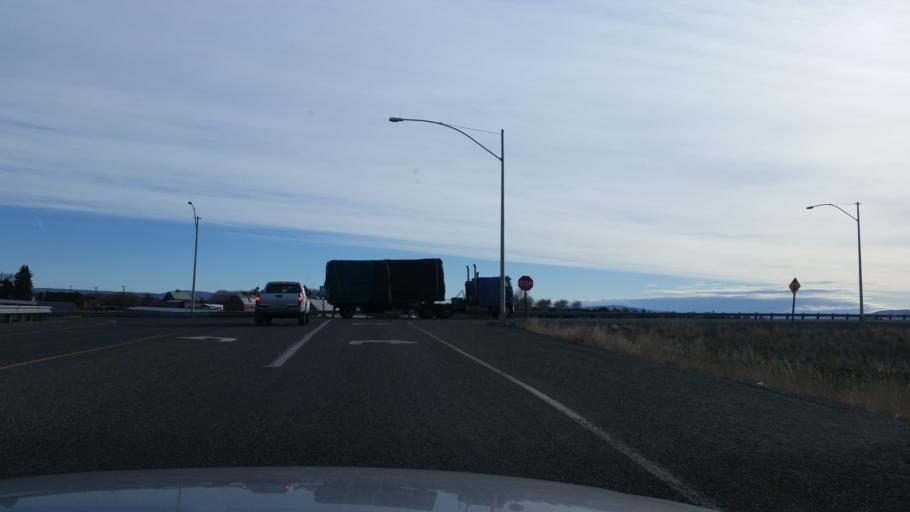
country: US
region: Washington
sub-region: Kittitas County
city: Ellensburg
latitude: 47.0122
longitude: -120.5758
